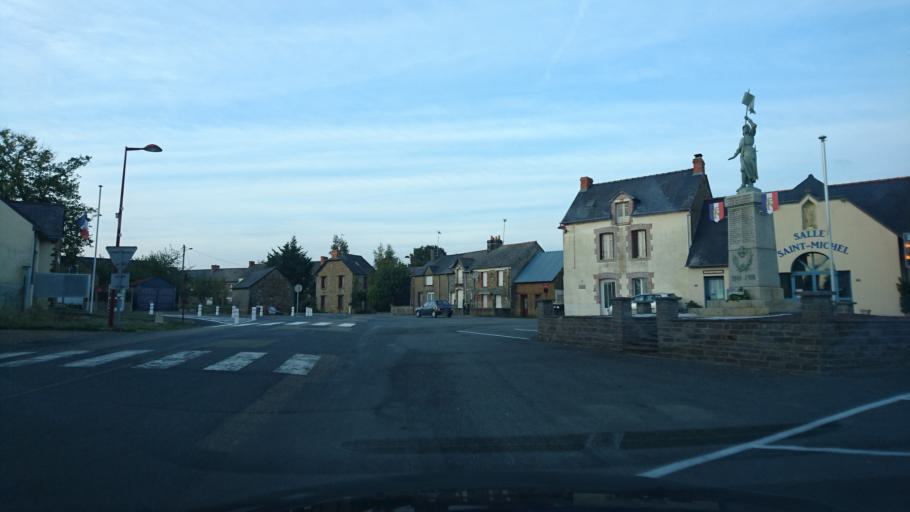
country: FR
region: Brittany
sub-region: Departement d'Ille-et-Vilaine
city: Maure-de-Bretagne
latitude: 47.8541
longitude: -2.0061
